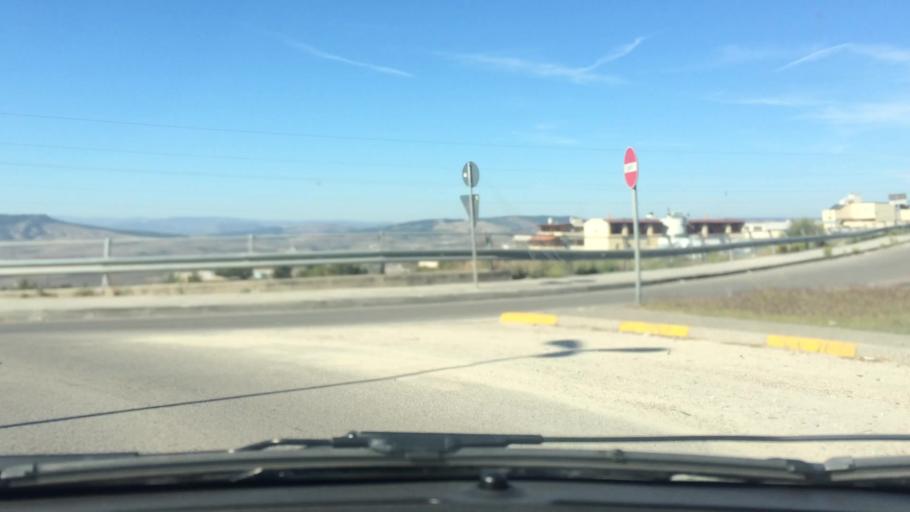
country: IT
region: Basilicate
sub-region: Provincia di Matera
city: Matera
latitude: 40.6752
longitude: 16.5763
